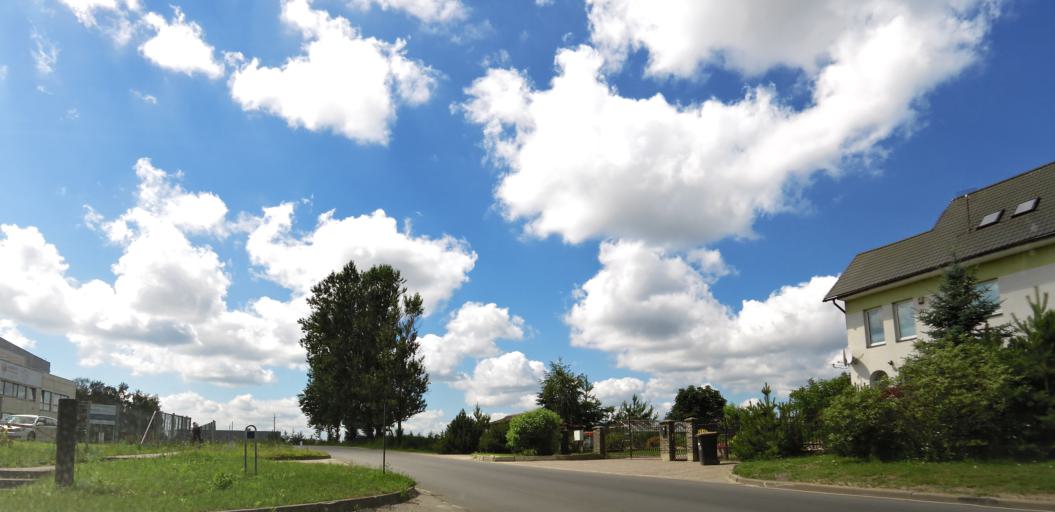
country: LT
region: Vilnius County
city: Pasilaiciai
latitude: 54.7351
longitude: 25.1876
